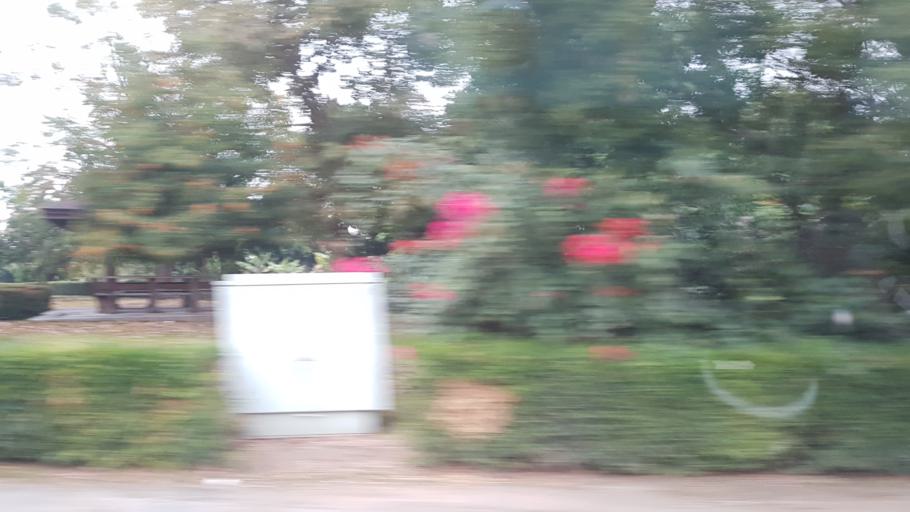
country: TW
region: Taiwan
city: Xinying
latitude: 23.3389
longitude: 120.3275
